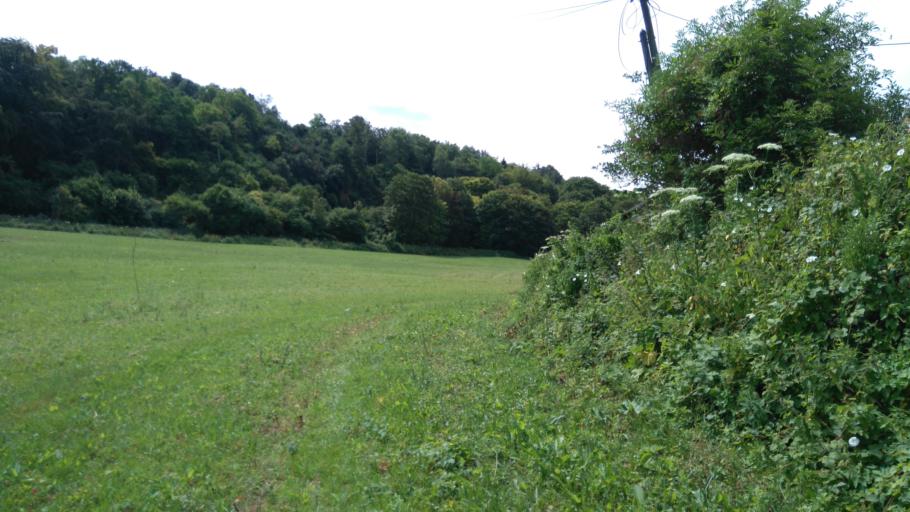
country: FR
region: Picardie
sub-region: Departement de l'Oise
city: Thiverny
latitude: 49.2441
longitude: 2.4543
